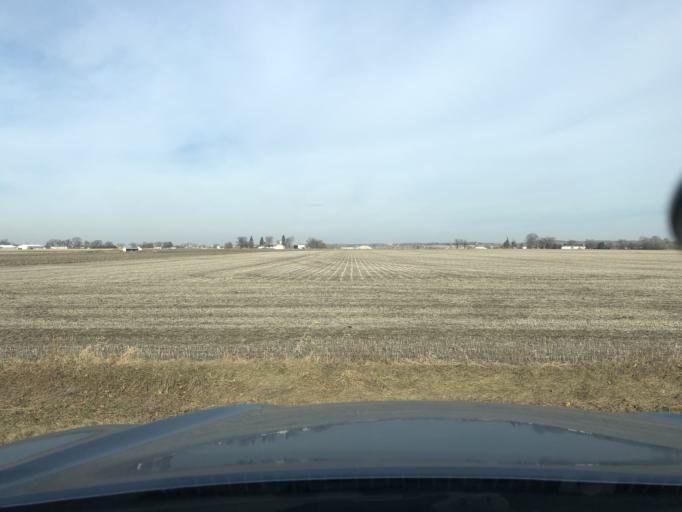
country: US
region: Illinois
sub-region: McHenry County
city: Marengo
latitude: 42.1824
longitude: -88.6125
